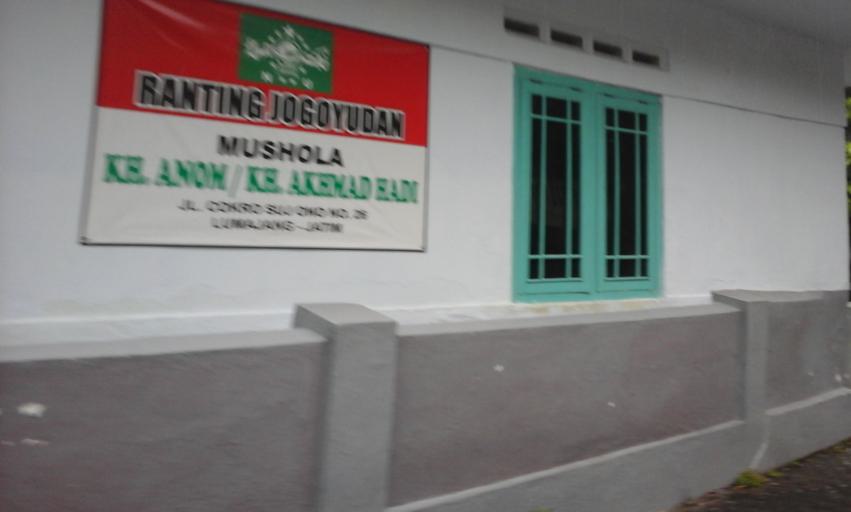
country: ID
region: East Java
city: Lumajang
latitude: -8.1347
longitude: 113.2270
